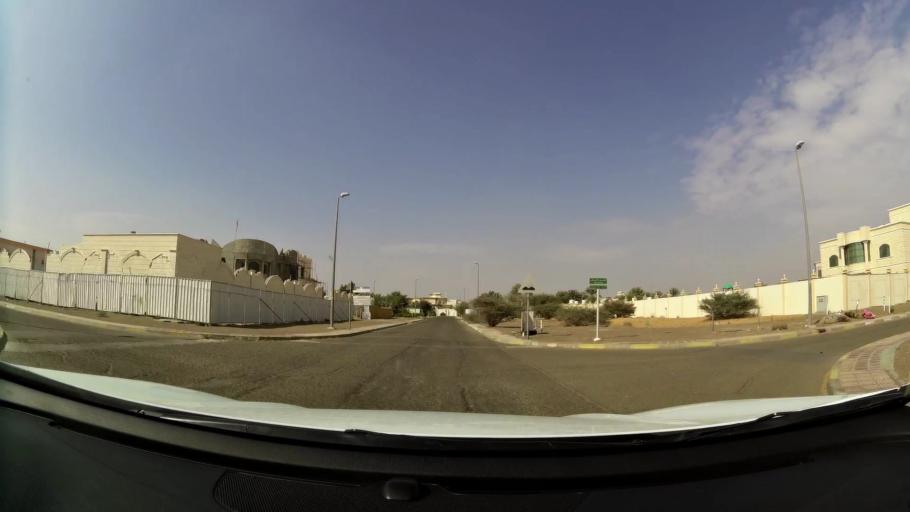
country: AE
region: Abu Dhabi
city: Al Ain
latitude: 24.0967
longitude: 55.9177
